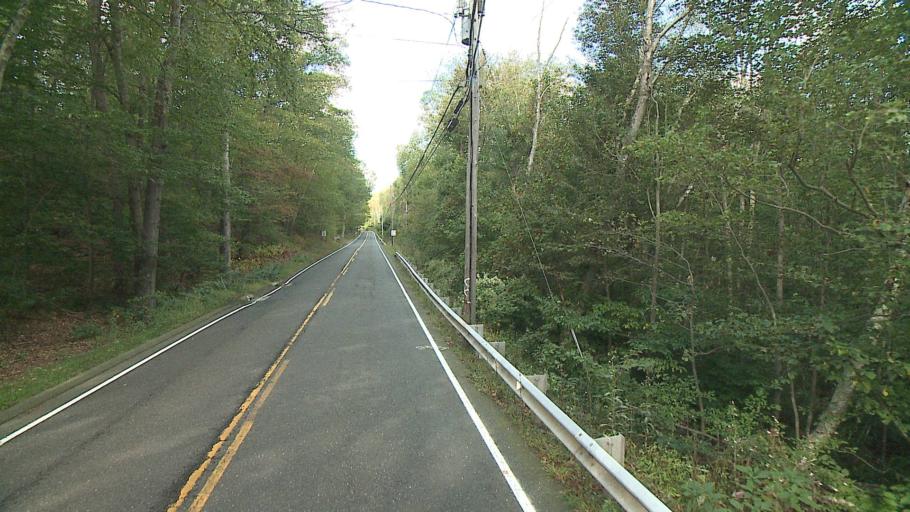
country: US
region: Connecticut
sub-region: New Haven County
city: Prospect
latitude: 41.4539
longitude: -72.9943
